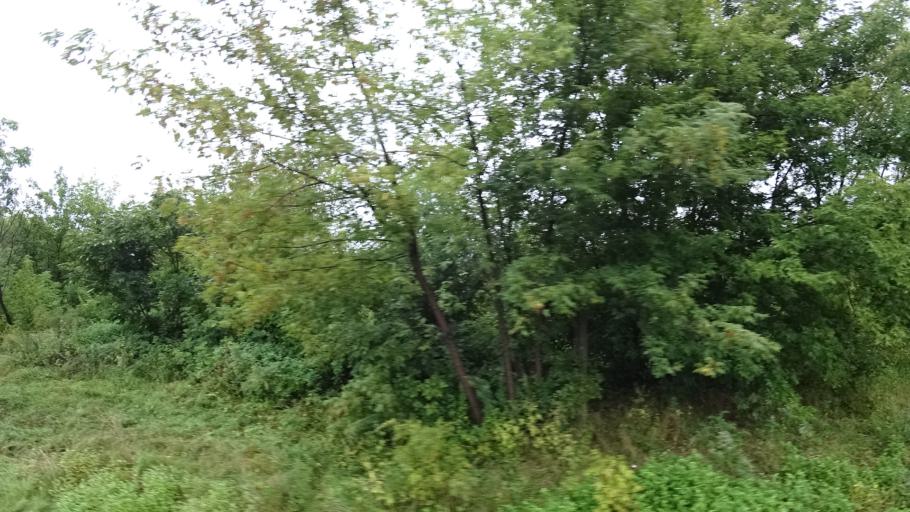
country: RU
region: Primorskiy
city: Monastyrishche
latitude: 44.2692
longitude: 132.4204
